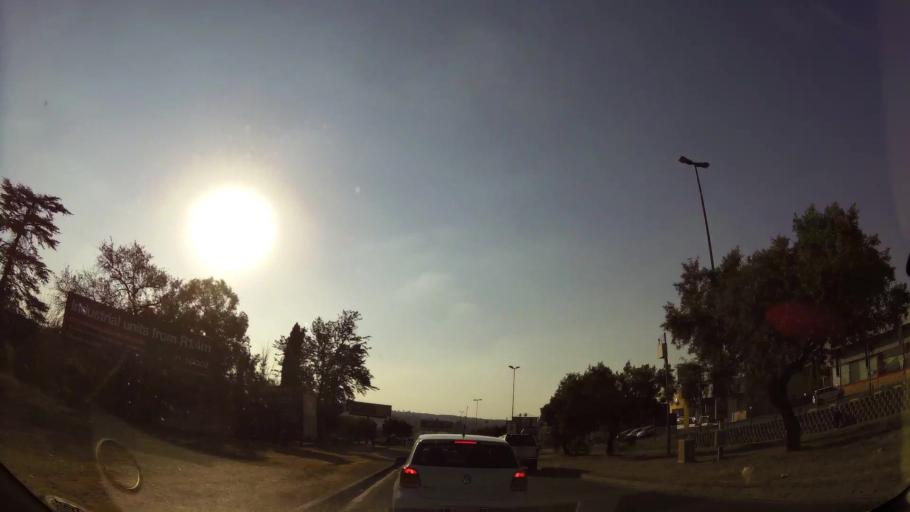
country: ZA
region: Gauteng
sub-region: City of Johannesburg Metropolitan Municipality
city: Roodepoort
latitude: -26.0783
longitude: 27.9761
